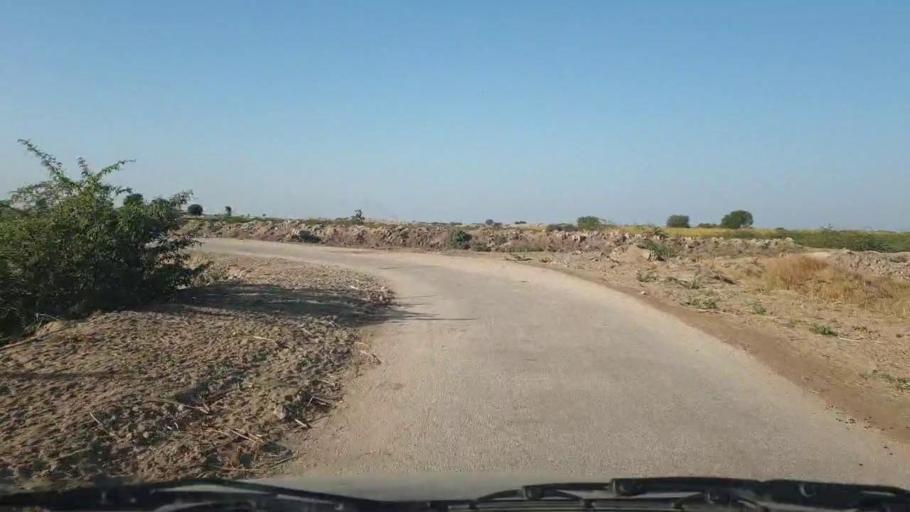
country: PK
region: Sindh
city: Samaro
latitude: 25.3513
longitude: 69.2984
